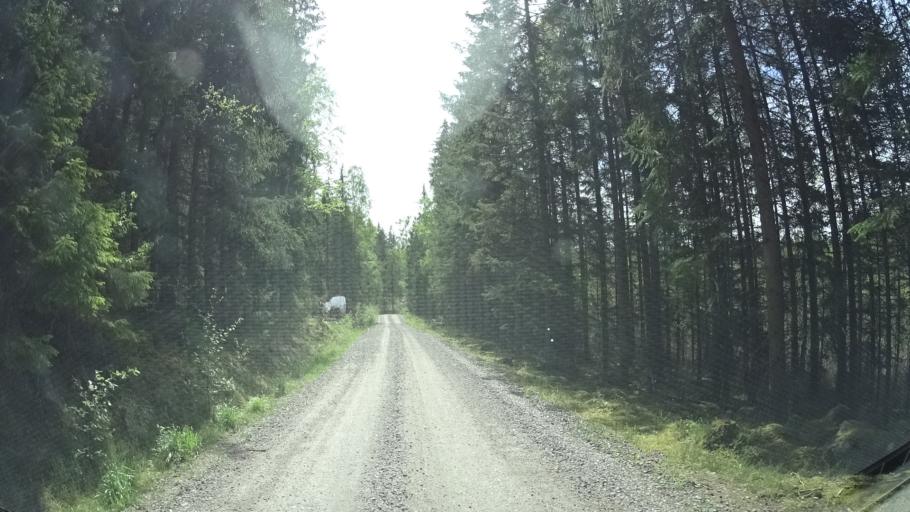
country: SE
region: OEstergoetland
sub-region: Finspangs Kommun
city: Finspang
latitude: 58.7885
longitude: 15.8454
